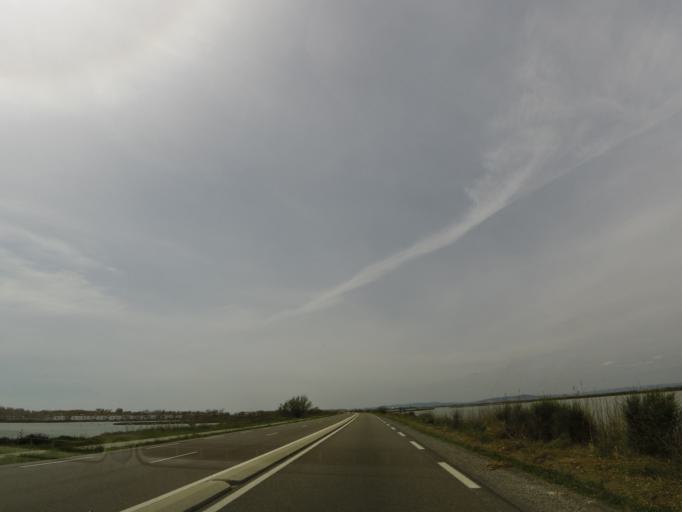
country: FR
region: Languedoc-Roussillon
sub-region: Departement de l'Herault
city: Perols
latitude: 43.5426
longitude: 3.9623
